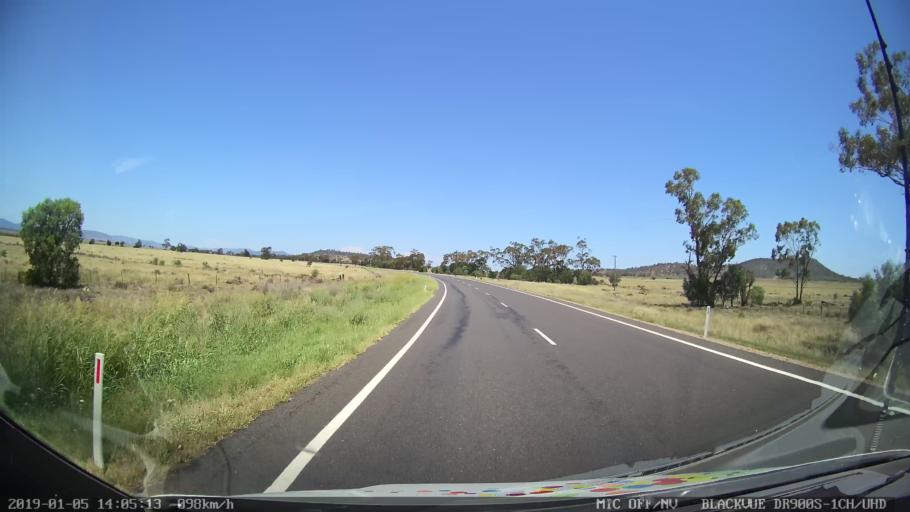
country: AU
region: New South Wales
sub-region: Gunnedah
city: Gunnedah
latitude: -31.2084
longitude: 150.3722
